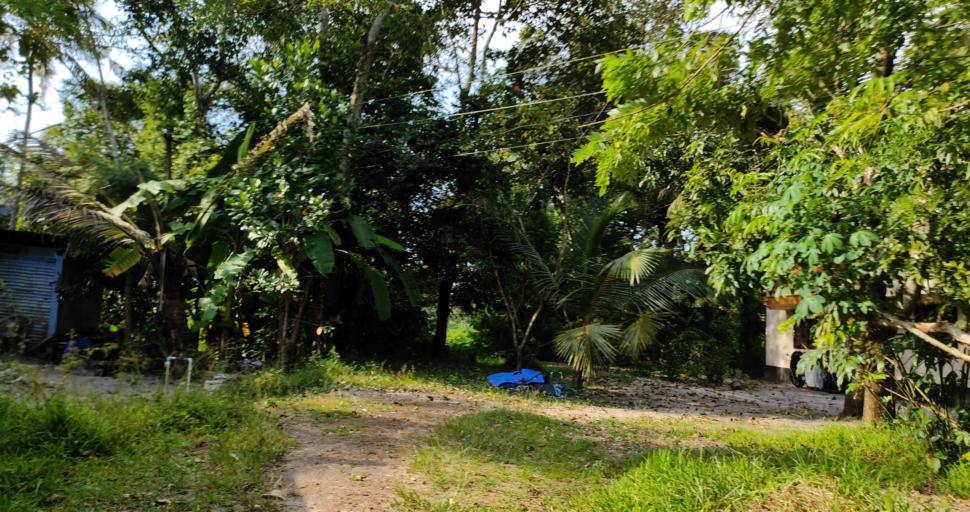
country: IN
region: Kerala
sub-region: Alappuzha
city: Shertallai
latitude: 9.6051
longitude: 76.3303
